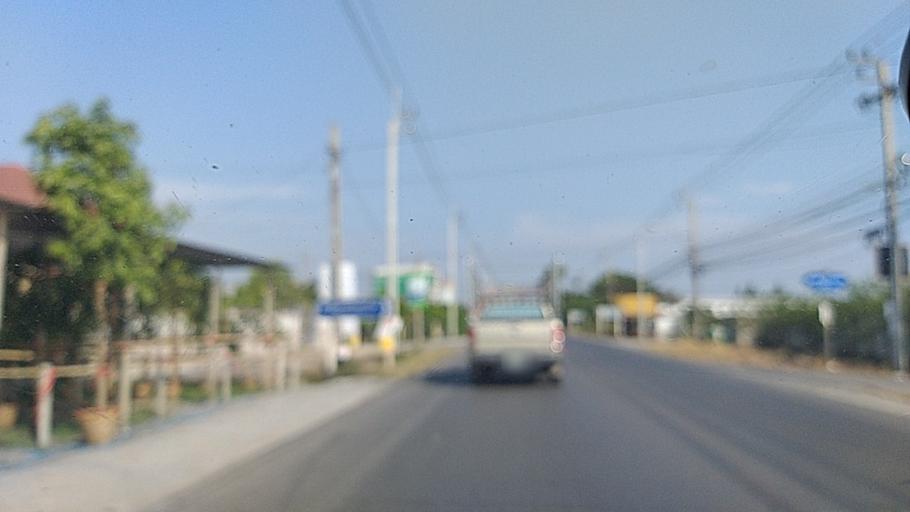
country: TH
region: Nonthaburi
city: Bang Bua Thong
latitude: 13.9355
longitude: 100.3698
